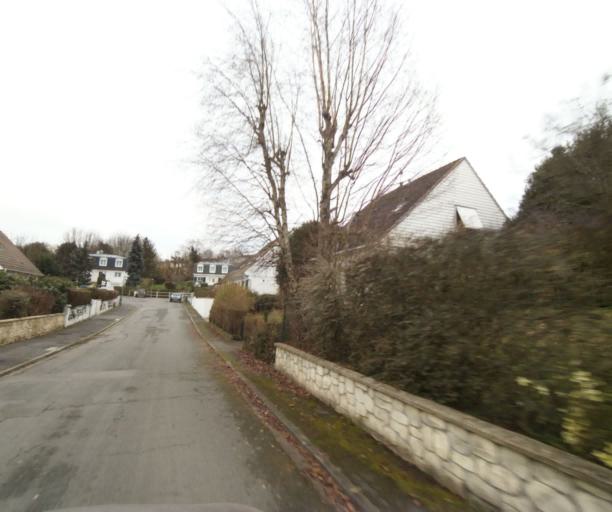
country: FR
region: Ile-de-France
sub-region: Departement de Seine-et-Marne
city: Dammartin-en-Goele
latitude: 49.0578
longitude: 2.6917
